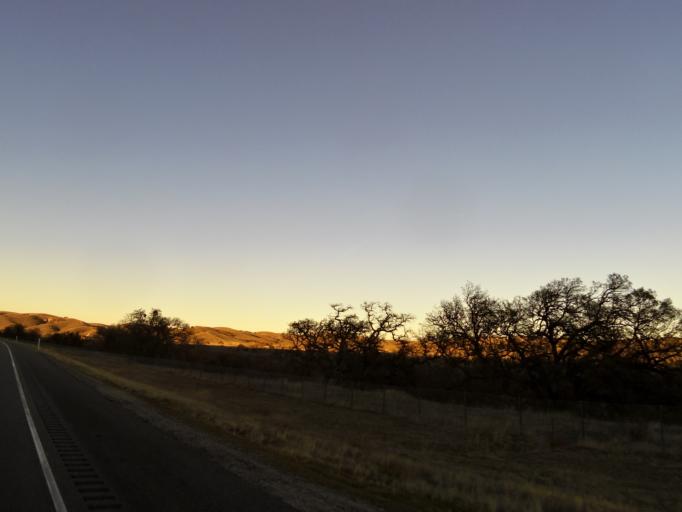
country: US
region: California
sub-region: San Luis Obispo County
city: San Miguel
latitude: 35.8368
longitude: -120.7578
